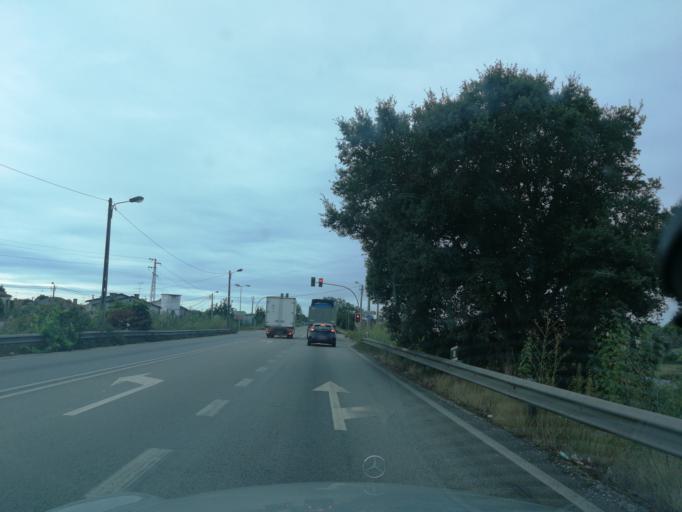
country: PT
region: Aveiro
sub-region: Agueda
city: Valongo
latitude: 40.6191
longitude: -8.4623
